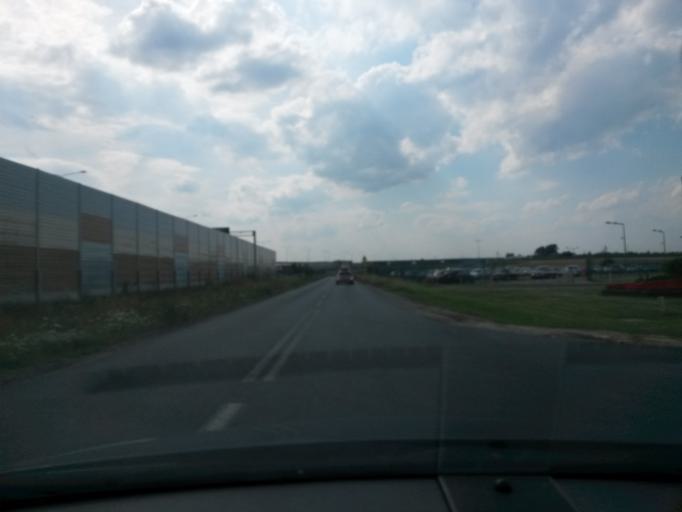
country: PL
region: Greater Poland Voivodeship
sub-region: Powiat poznanski
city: Kornik
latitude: 52.2568
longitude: 17.0862
